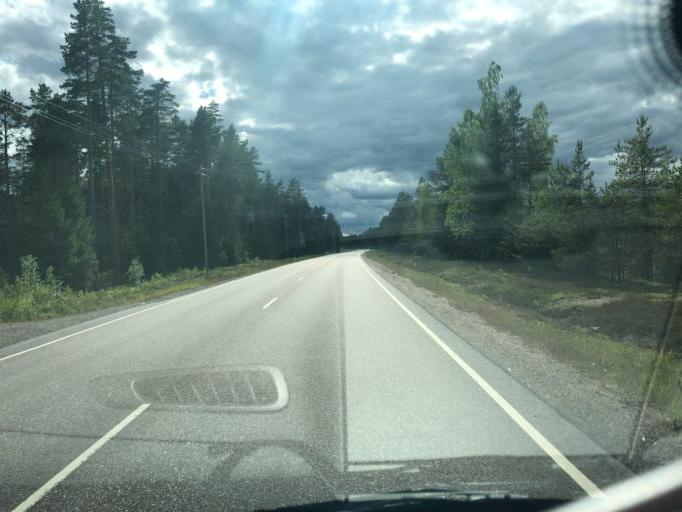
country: FI
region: Southern Savonia
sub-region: Mikkeli
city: Maentyharju
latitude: 61.0949
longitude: 27.0823
